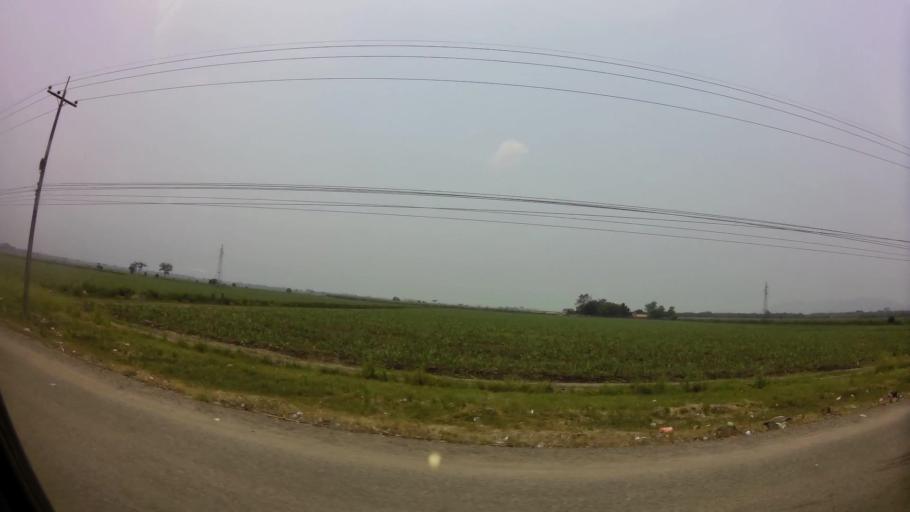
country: HN
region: Cortes
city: La Lima
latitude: 15.4117
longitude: -87.8617
